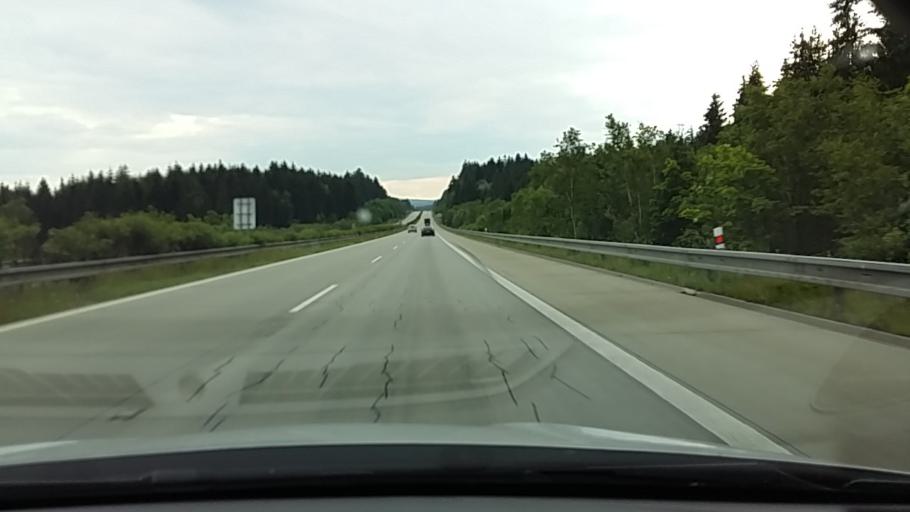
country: CZ
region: Plzensky
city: Primda
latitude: 49.6804
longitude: 12.6383
